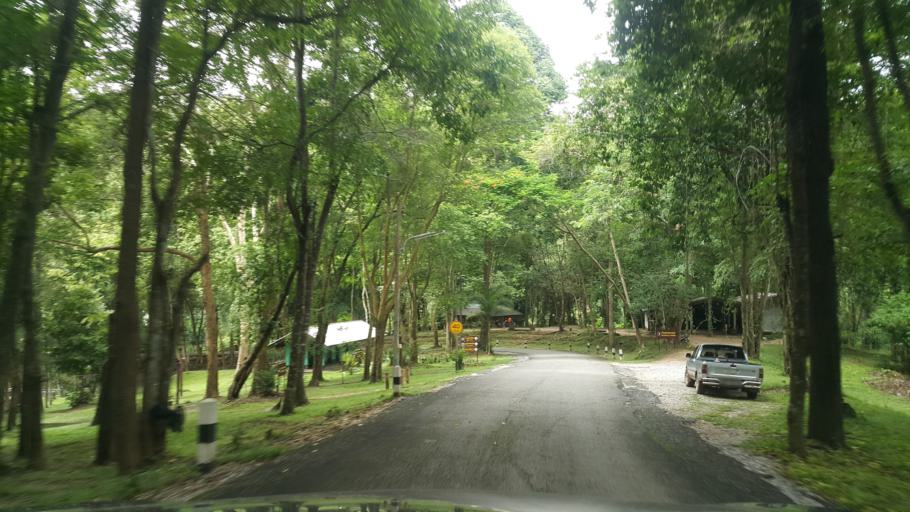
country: TH
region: Phitsanulok
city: Chat Trakan
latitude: 17.3013
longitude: 100.6787
